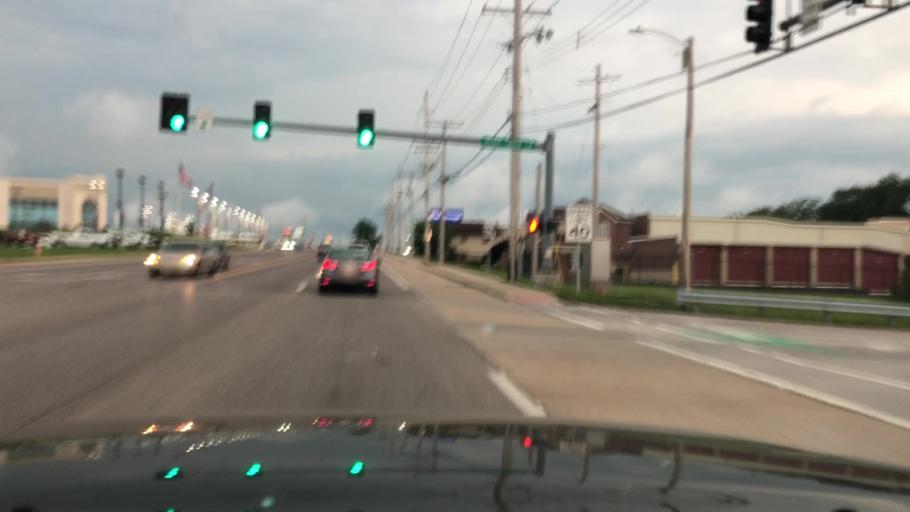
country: US
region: Missouri
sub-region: Saint Louis County
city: Bridgeton
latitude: 38.7425
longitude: -90.4090
